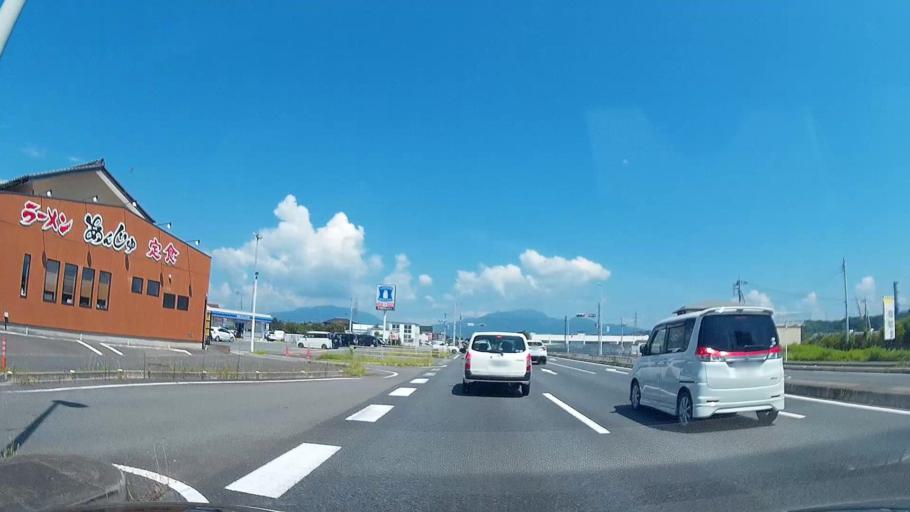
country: JP
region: Gunma
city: Shibukawa
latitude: 36.4696
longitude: 139.0247
